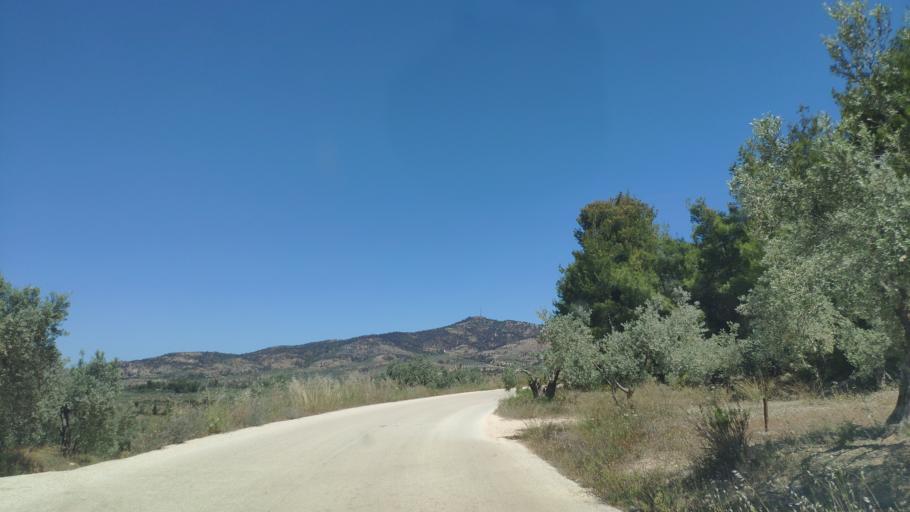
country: GR
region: Peloponnese
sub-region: Nomos Korinthias
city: Athikia
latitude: 37.8321
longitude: 22.9279
